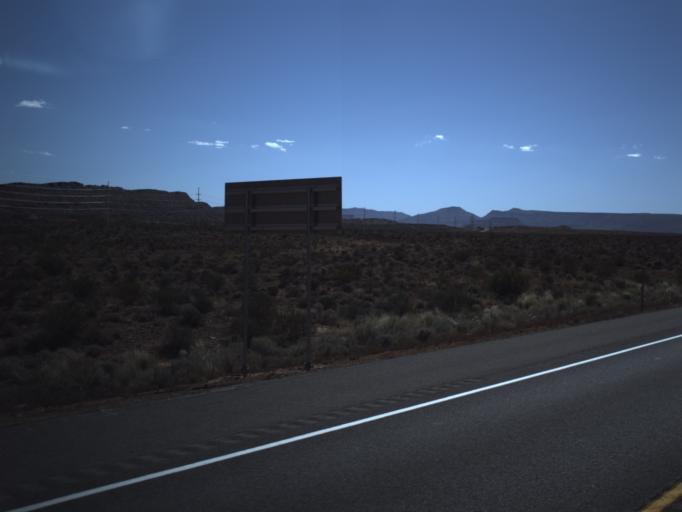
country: US
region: Utah
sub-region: Washington County
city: Washington
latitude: 37.0449
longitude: -113.4857
